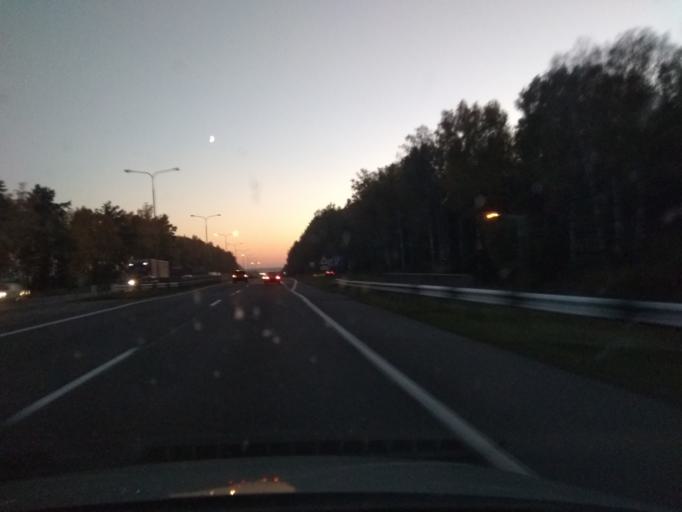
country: BY
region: Minsk
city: Enyerhyetykaw
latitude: 53.6379
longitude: 27.0647
